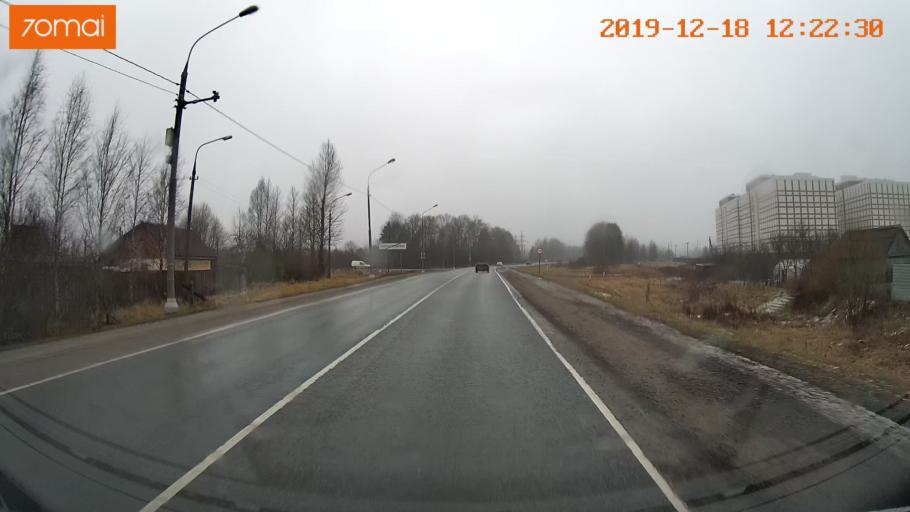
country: RU
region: Moskovskaya
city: Novopetrovskoye
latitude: 56.0064
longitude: 36.4811
